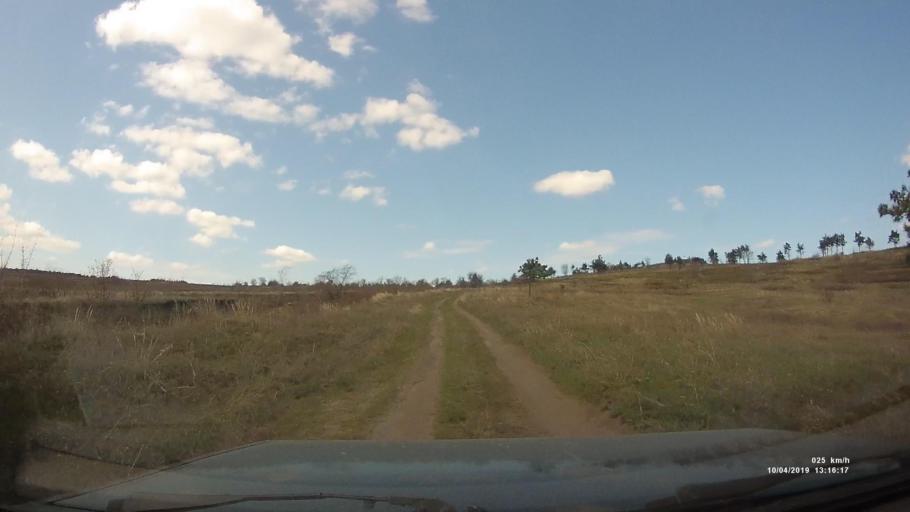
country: RU
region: Rostov
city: Masalovka
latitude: 48.4201
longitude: 40.2564
